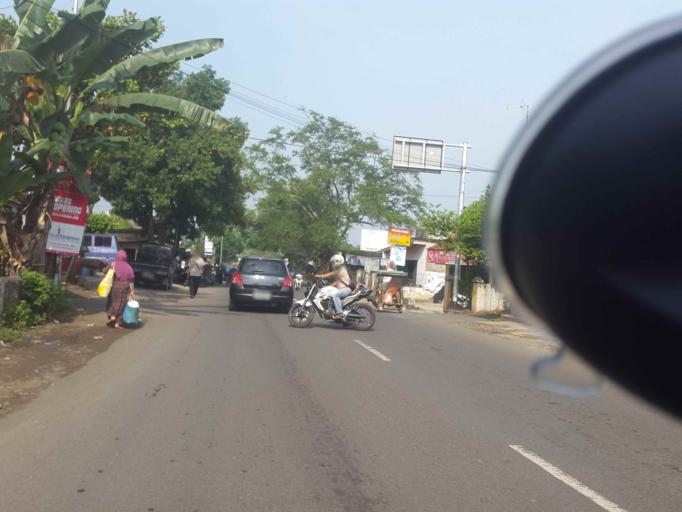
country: ID
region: Central Java
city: Sokaraja
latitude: -7.4577
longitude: 109.2872
